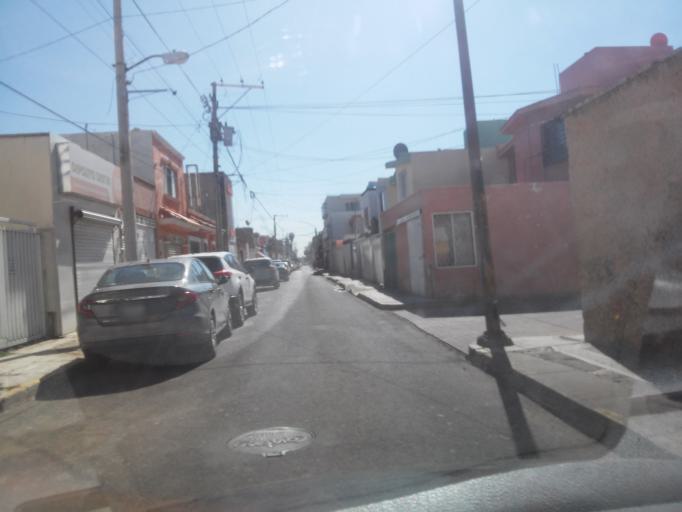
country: MX
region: Durango
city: Victoria de Durango
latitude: 24.0319
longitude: -104.6651
